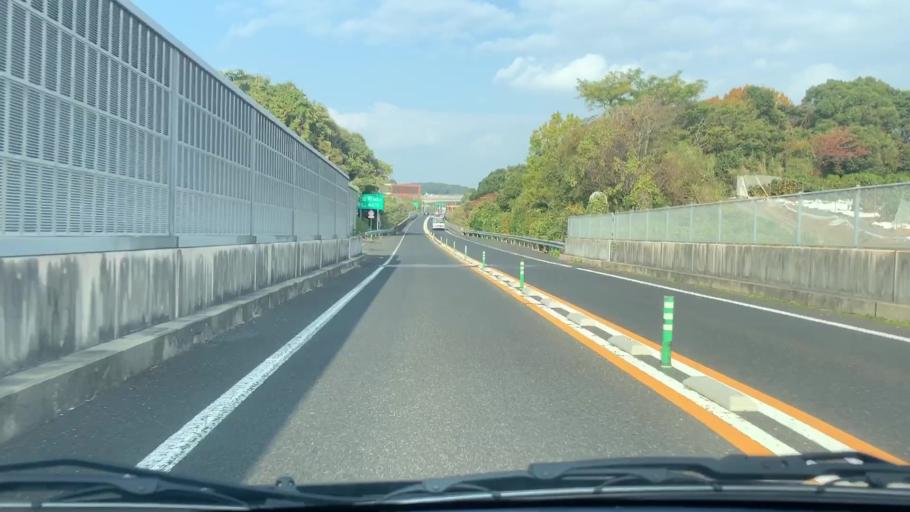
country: JP
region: Nagasaki
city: Sasebo
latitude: 33.0603
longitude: 129.7589
